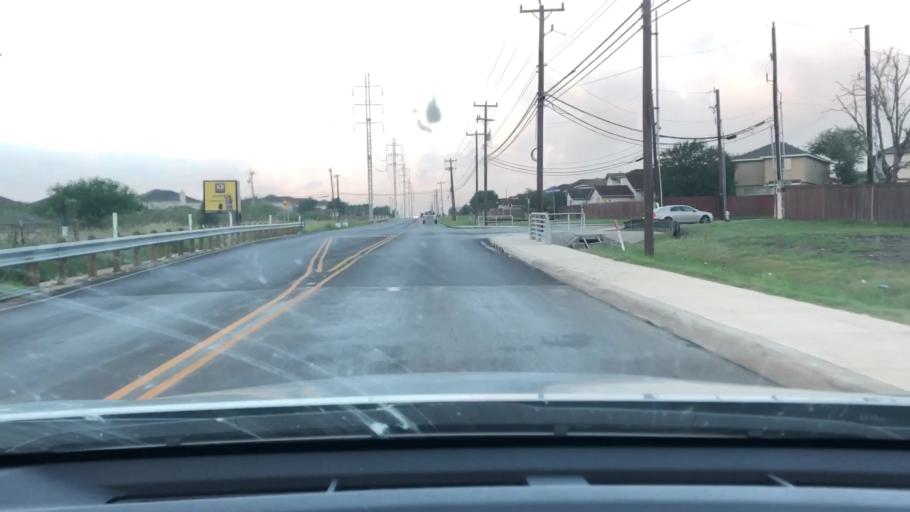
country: US
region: Texas
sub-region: Bexar County
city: Kirby
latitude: 29.4653
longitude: -98.3516
